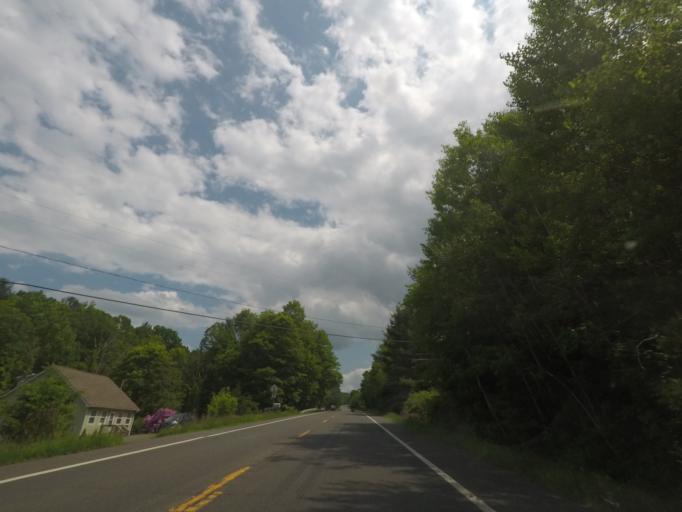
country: US
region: New York
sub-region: Dutchess County
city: Pine Plains
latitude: 42.1071
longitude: -73.6936
